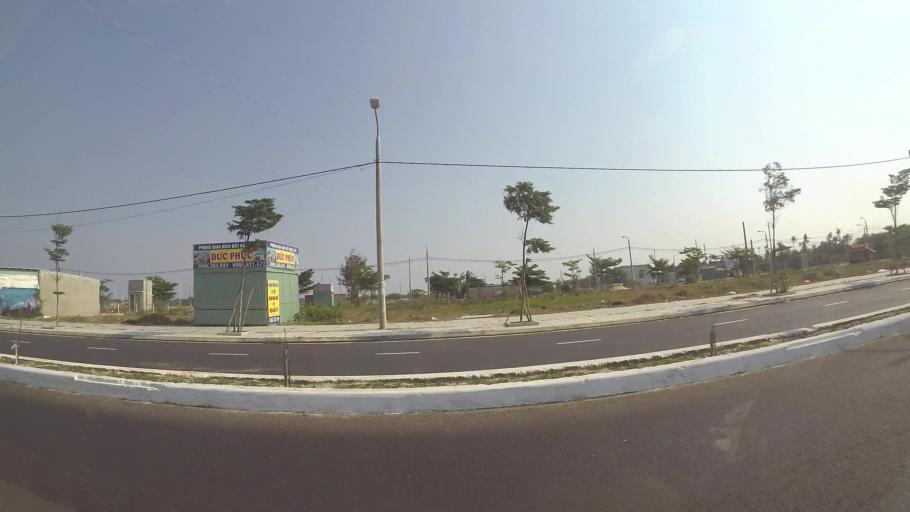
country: VN
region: Da Nang
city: Ngu Hanh Son
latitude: 15.9542
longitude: 108.2809
